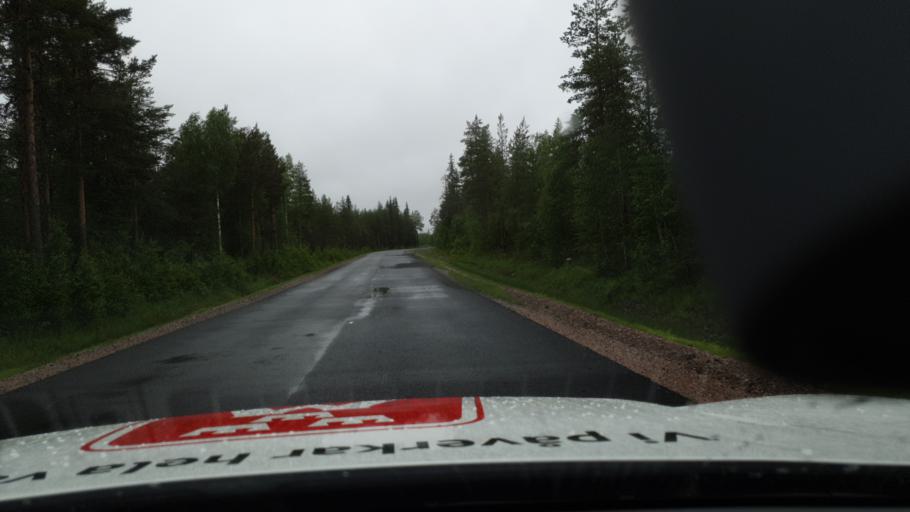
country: SE
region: Norrbotten
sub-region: Overtornea Kommun
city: OEvertornea
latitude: 66.5560
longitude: 23.3382
